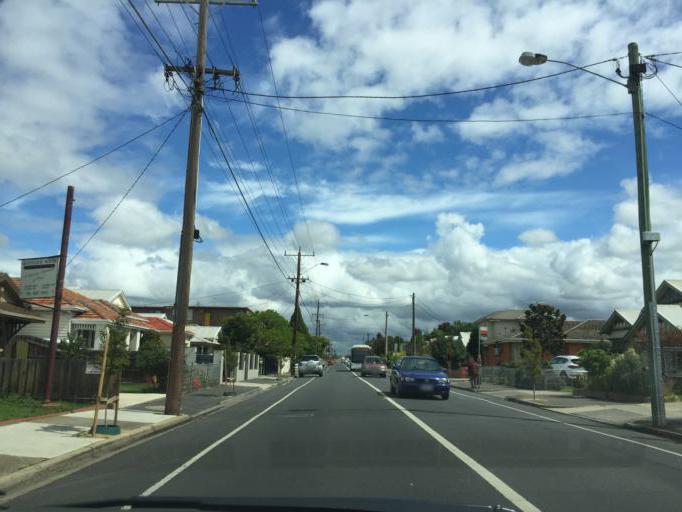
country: AU
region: Victoria
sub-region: Maribyrnong
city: West Footscray
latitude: -37.7969
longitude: 144.8723
